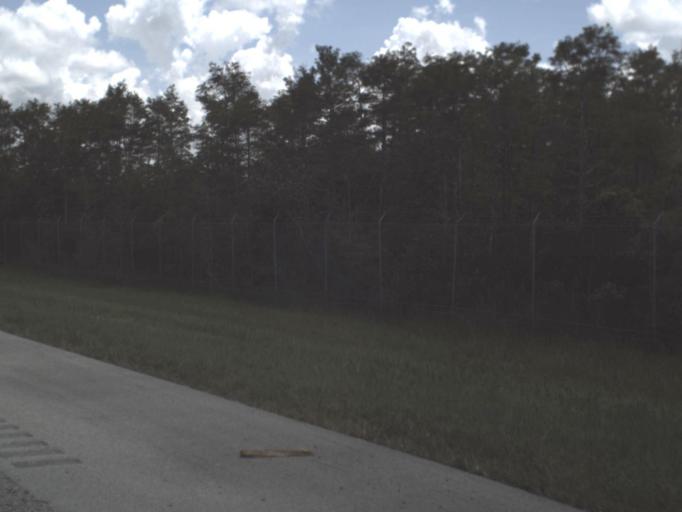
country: US
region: Florida
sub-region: Broward County
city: Weston
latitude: 26.1718
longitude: -80.9136
